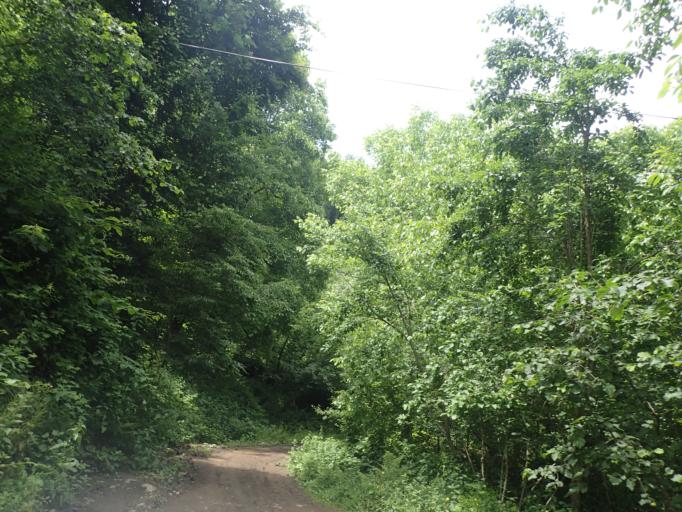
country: TR
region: Samsun
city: Salipazari
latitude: 40.9481
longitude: 36.9283
